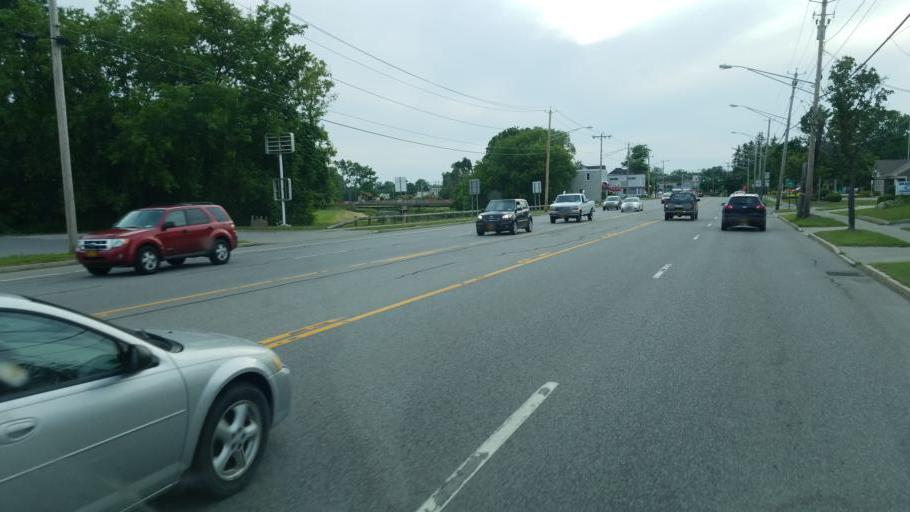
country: US
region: New York
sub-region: Genesee County
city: Batavia
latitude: 43.0037
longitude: -78.2000
